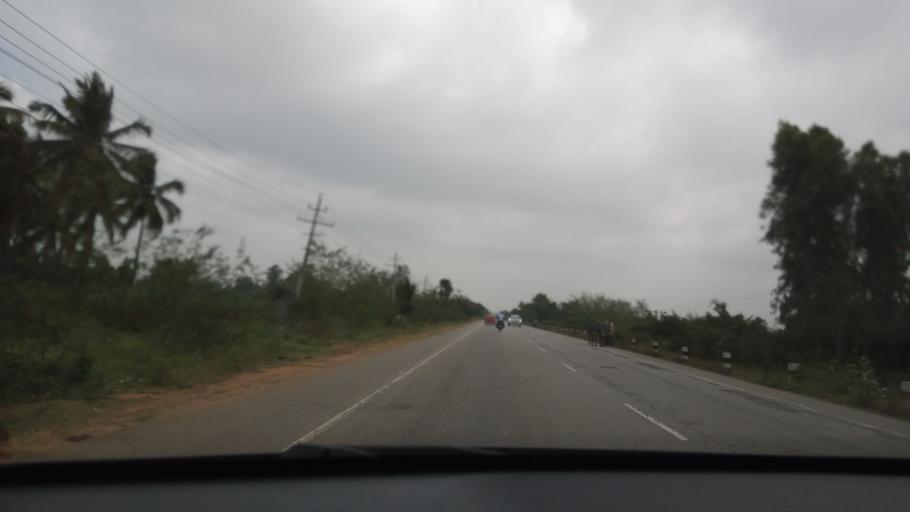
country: IN
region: Karnataka
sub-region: Chikkaballapur
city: Chintamani
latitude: 13.3401
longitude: 78.0094
